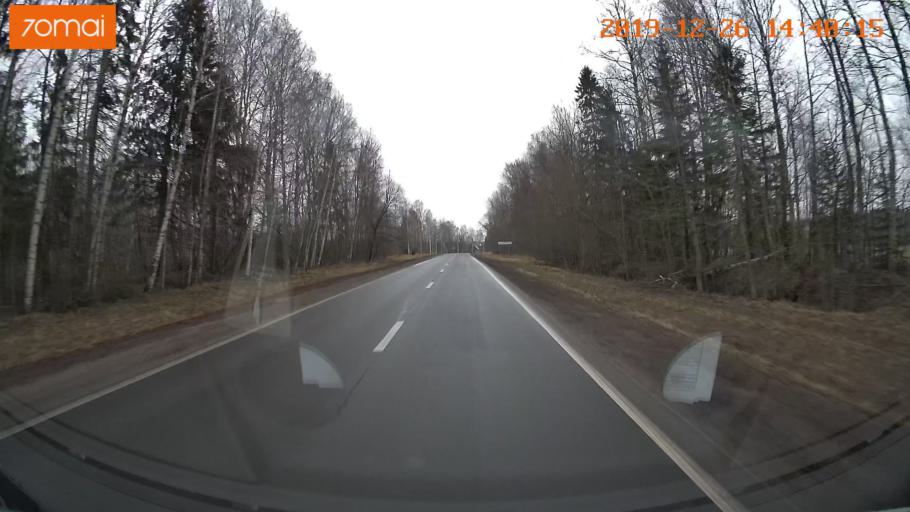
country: RU
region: Jaroslavl
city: Poshekhon'ye
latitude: 58.3771
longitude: 38.9954
